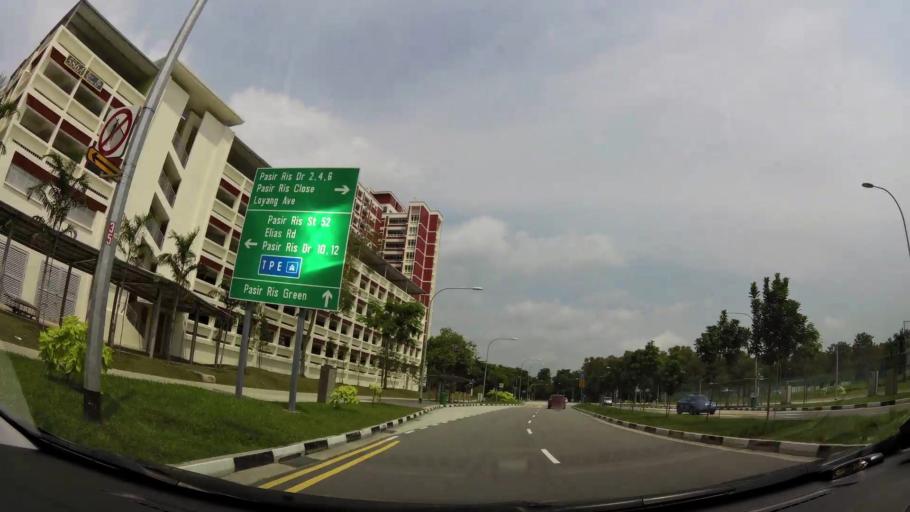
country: MY
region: Johor
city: Kampung Pasir Gudang Baru
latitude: 1.3744
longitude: 103.9479
